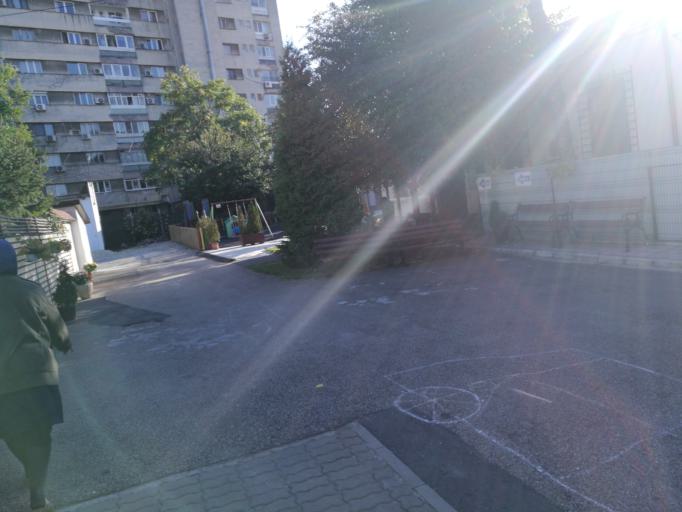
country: RO
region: Bucuresti
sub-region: Municipiul Bucuresti
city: Bucharest
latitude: 44.4428
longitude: 26.1064
